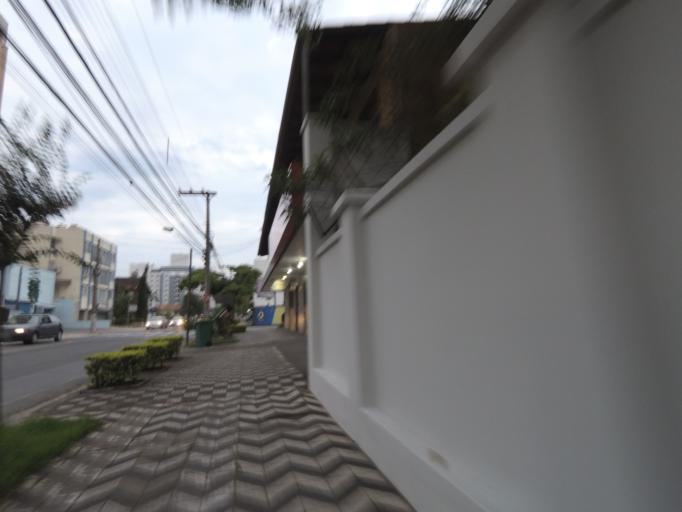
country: BR
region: Santa Catarina
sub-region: Blumenau
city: Blumenau
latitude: -26.9147
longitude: -49.0660
